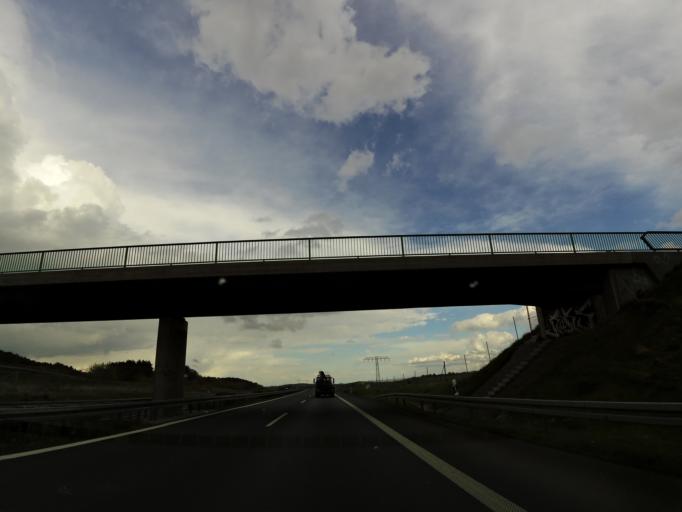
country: DE
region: Saxony-Anhalt
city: Blankenburg
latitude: 51.8065
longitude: 10.9585
